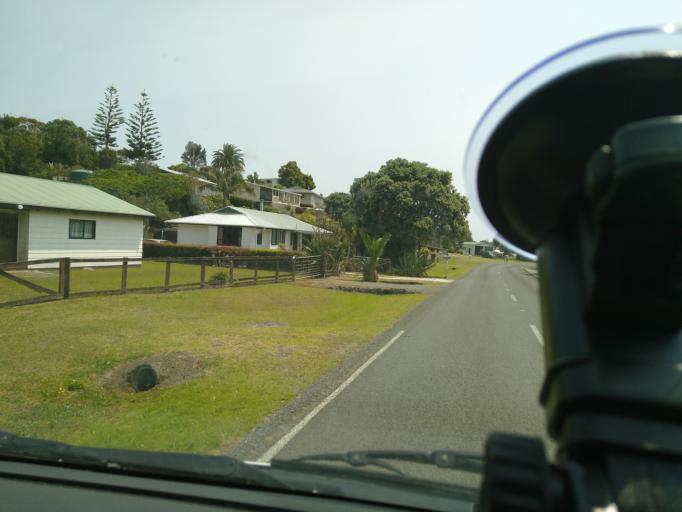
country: NZ
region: Northland
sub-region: Far North District
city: Kaitaia
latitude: -34.8168
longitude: 173.1163
